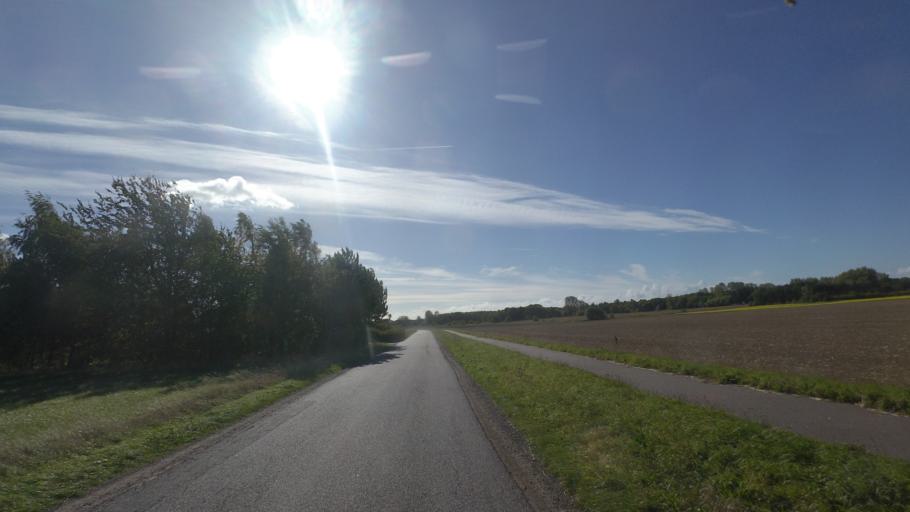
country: DK
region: Capital Region
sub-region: Bornholm Kommune
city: Akirkeby
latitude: 55.0150
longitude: 14.9917
